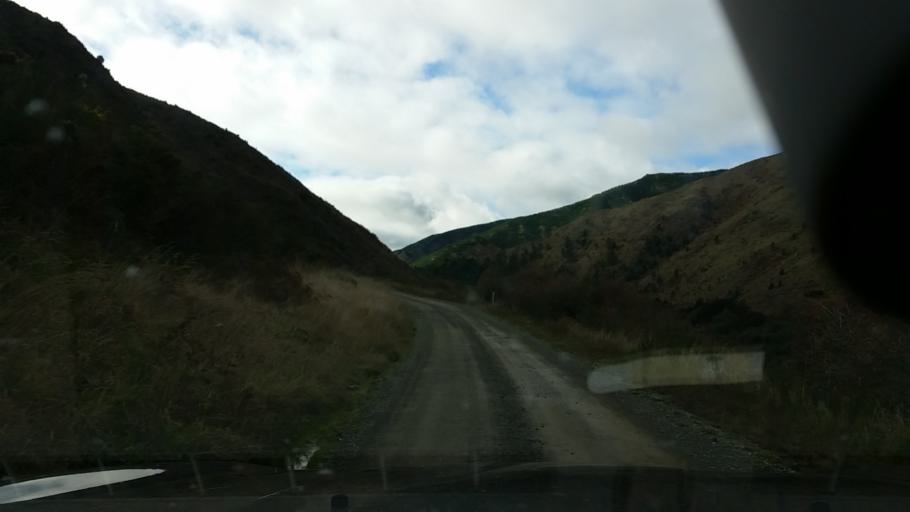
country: NZ
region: Tasman
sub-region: Tasman District
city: Richmond
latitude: -41.7147
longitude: 173.4777
